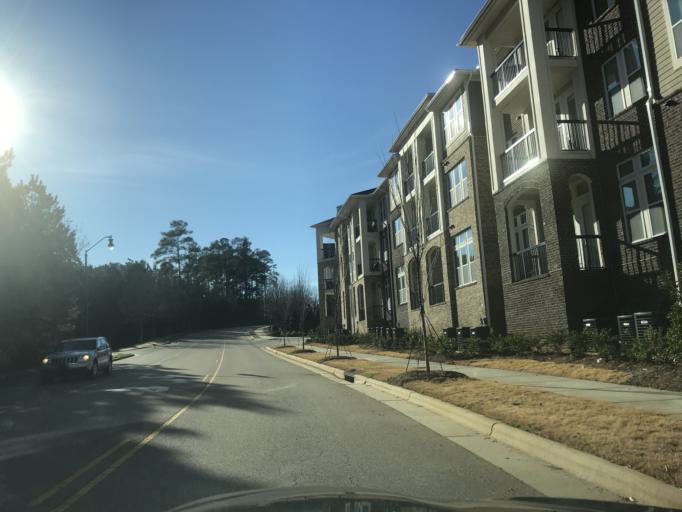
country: US
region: North Carolina
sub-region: Wake County
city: Cary
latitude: 35.8053
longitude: -78.7290
